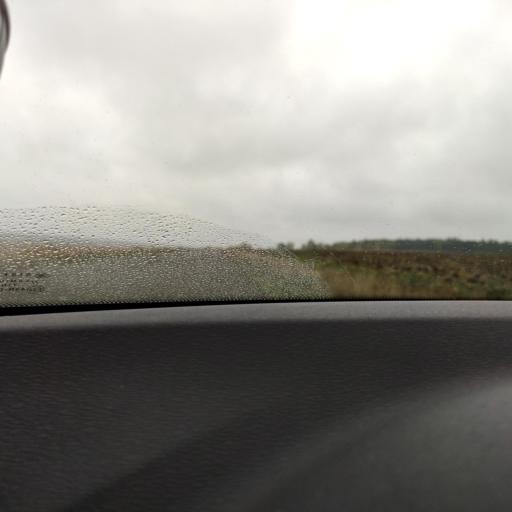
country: RU
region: Samara
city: Yelkhovka
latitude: 53.7429
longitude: 50.2320
